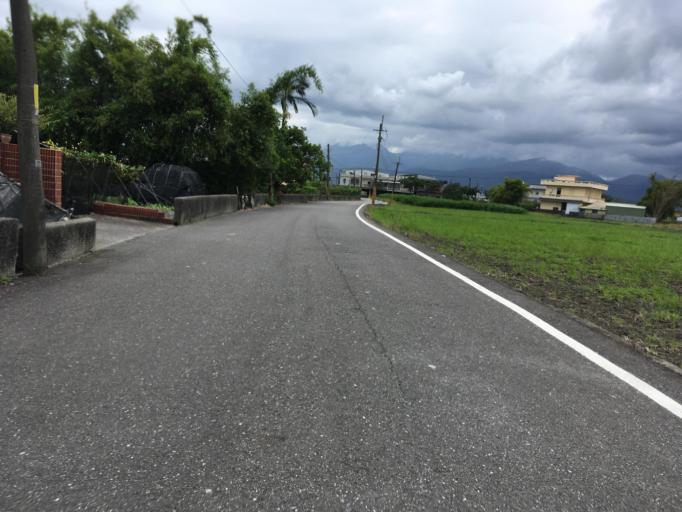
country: TW
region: Taiwan
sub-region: Yilan
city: Yilan
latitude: 24.6863
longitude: 121.8033
